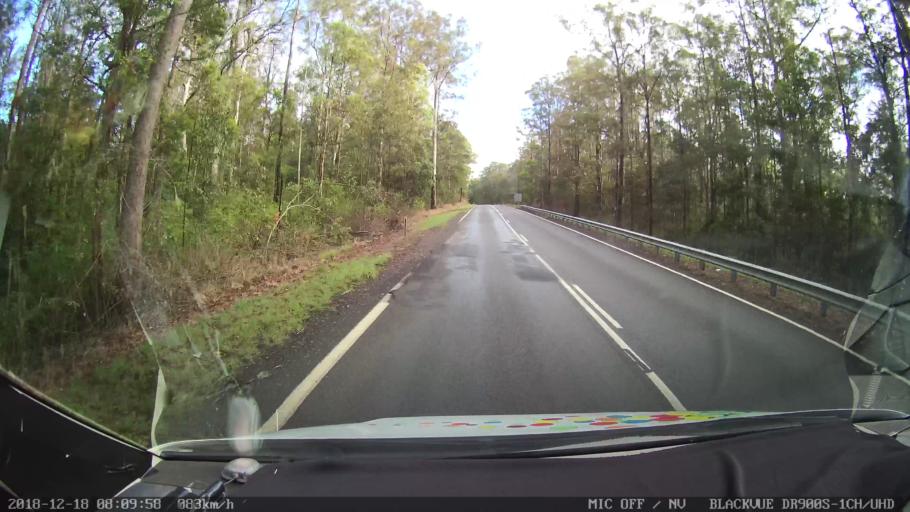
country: AU
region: New South Wales
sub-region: Kyogle
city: Kyogle
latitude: -28.3669
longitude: 152.6593
